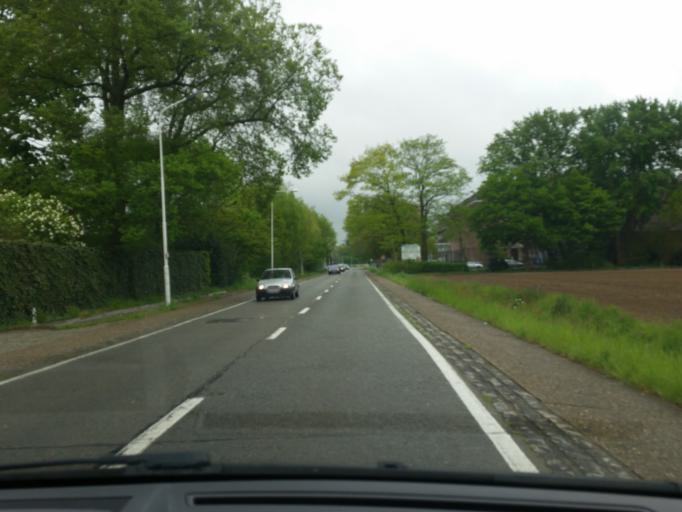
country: BE
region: Flanders
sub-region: Provincie Antwerpen
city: Boechout
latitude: 51.1735
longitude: 4.4892
